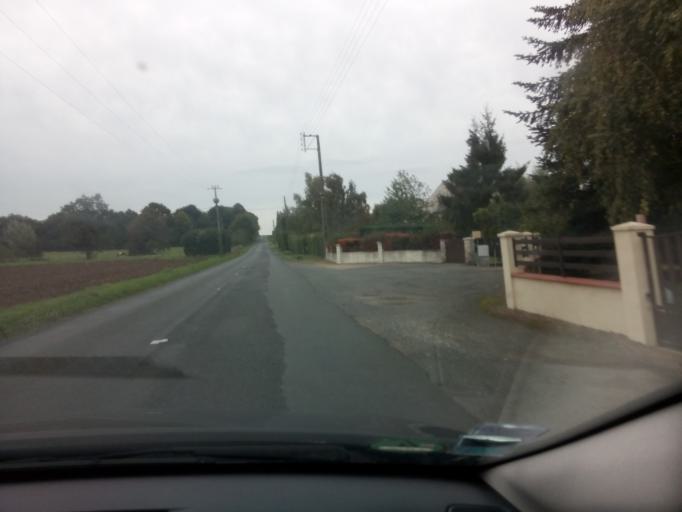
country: FR
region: Pays de la Loire
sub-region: Departement de Maine-et-Loire
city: Corne
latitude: 47.4830
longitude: -0.3389
